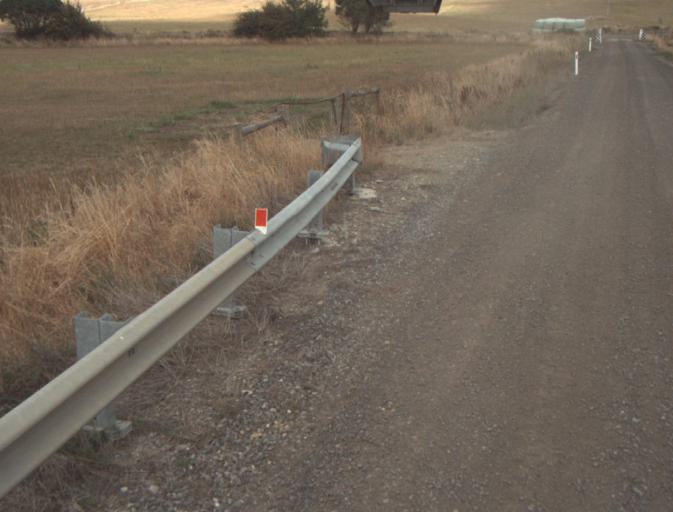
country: AU
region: Tasmania
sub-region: Launceston
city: Mayfield
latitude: -41.2125
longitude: 147.1492
